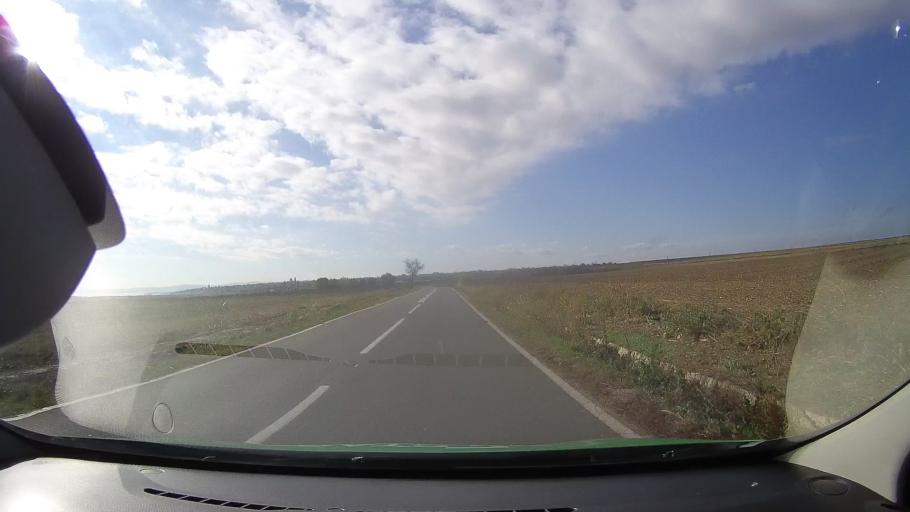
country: RO
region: Tulcea
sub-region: Comuna Sarichioi
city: Sarichioi
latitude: 44.9631
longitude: 28.8619
